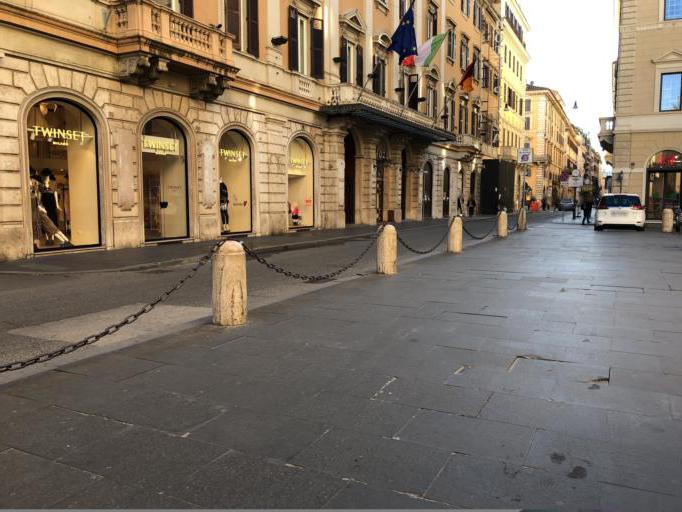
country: VA
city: Vatican City
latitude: 41.9053
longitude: 12.4785
